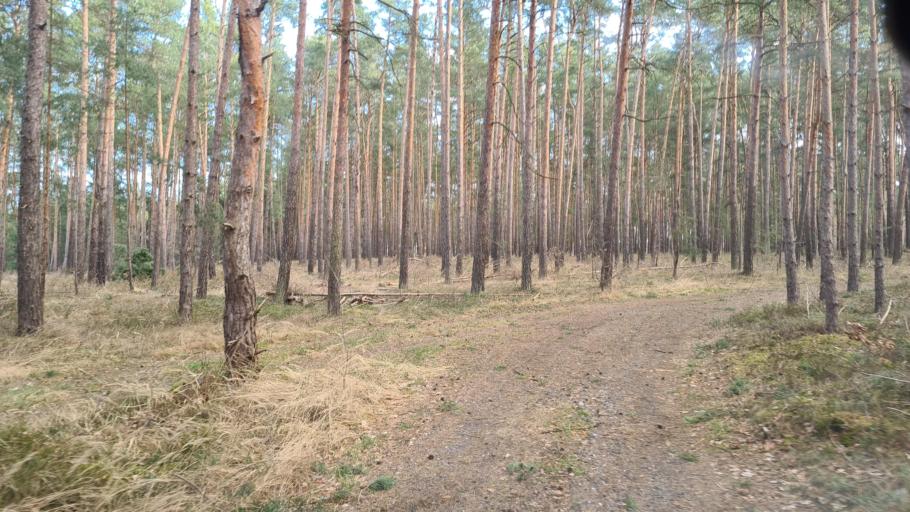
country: DE
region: Brandenburg
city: Finsterwalde
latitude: 51.5574
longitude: 13.6597
